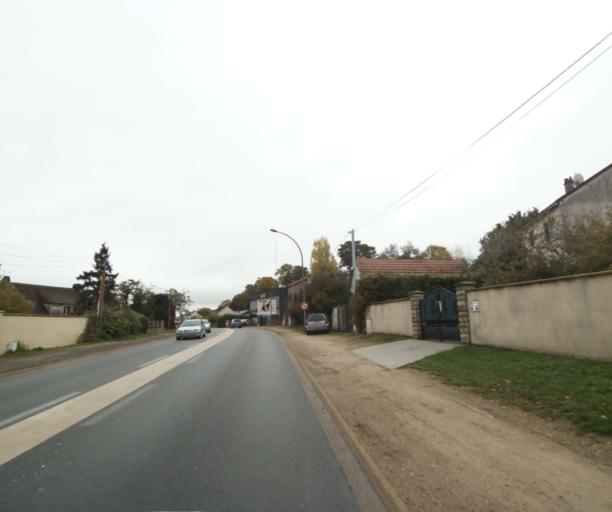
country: FR
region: Centre
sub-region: Departement d'Eure-et-Loir
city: Dreux
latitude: 48.7389
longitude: 1.3850
